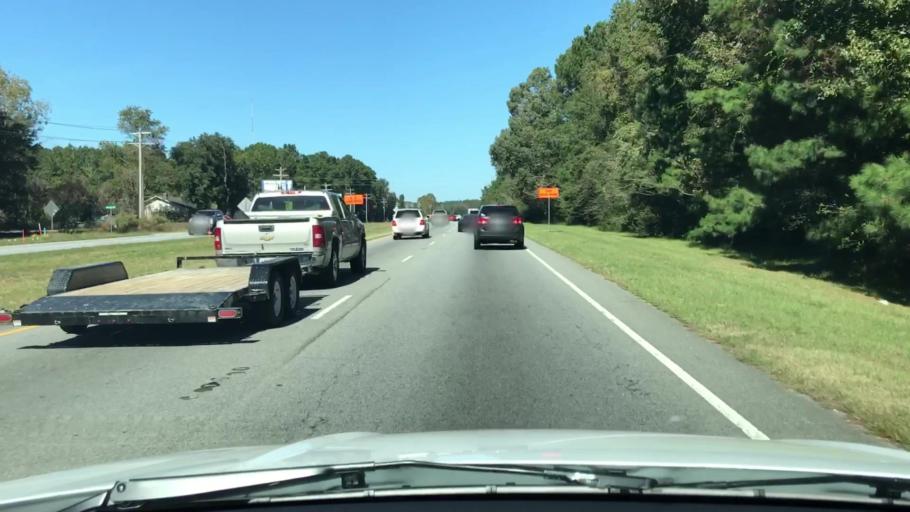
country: US
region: South Carolina
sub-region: Beaufort County
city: Bluffton
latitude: 32.3139
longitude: -80.9345
